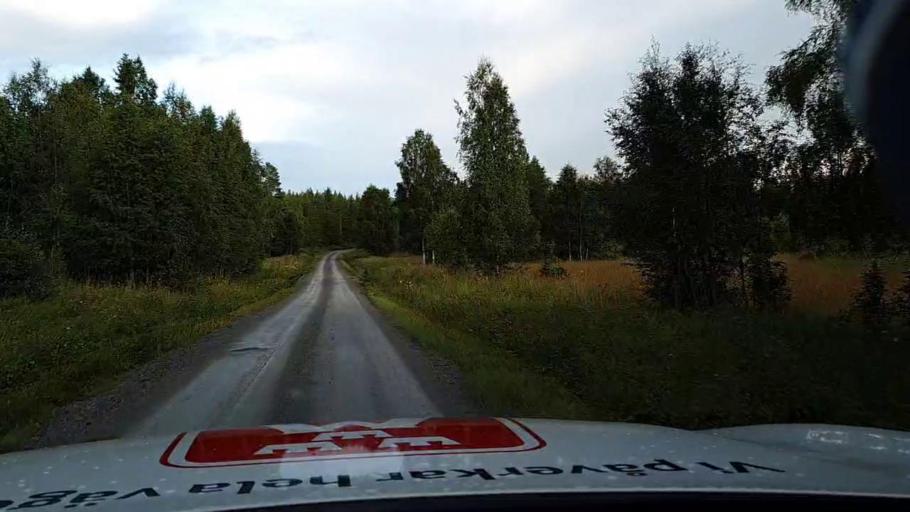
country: SE
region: Jaemtland
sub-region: Bergs Kommun
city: Hoverberg
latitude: 62.8659
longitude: 14.5274
